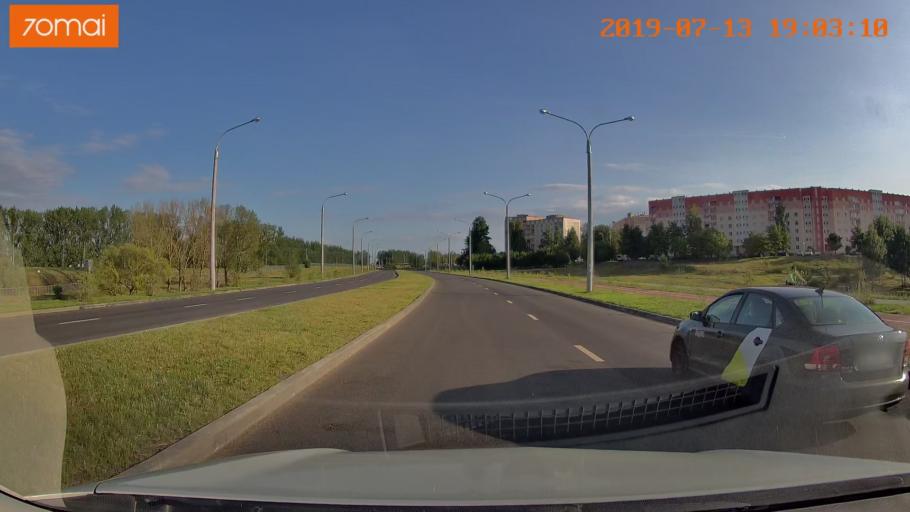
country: BY
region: Minsk
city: Syenitsa
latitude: 53.8559
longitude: 27.5560
